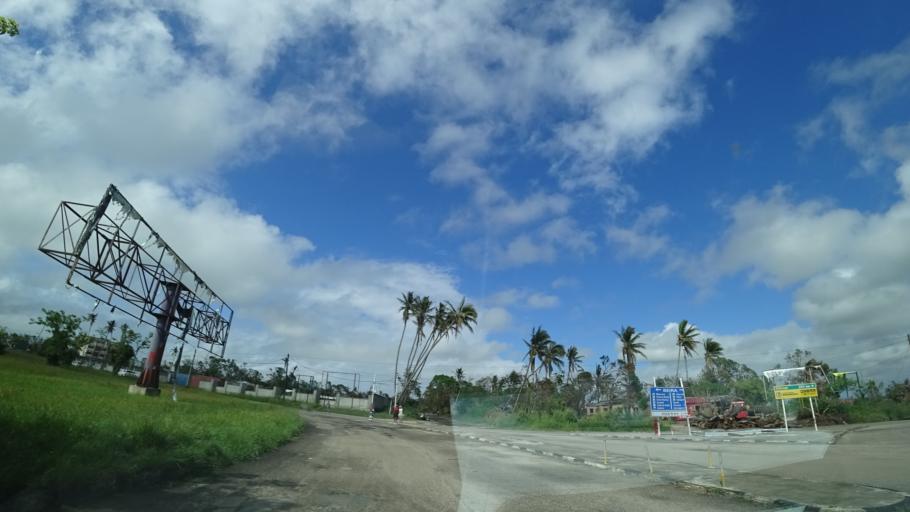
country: MZ
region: Sofala
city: Beira
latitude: -19.8009
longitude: 34.8999
